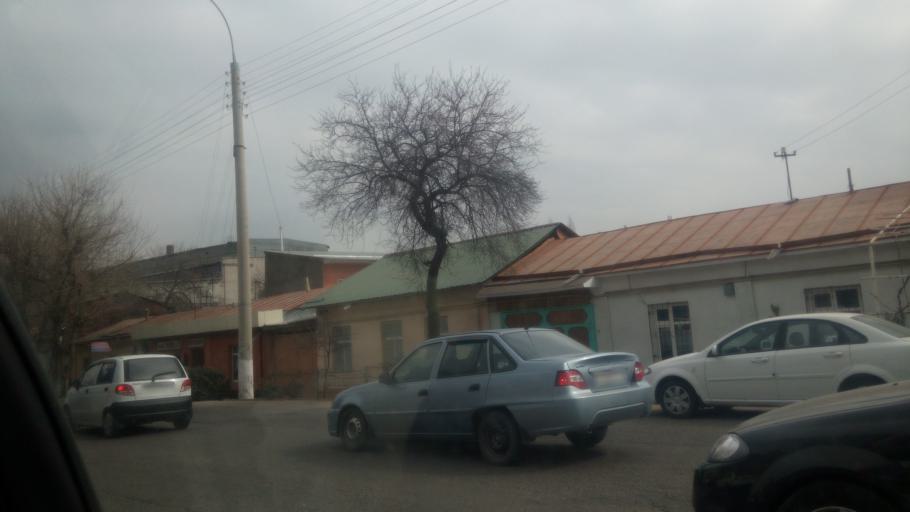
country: UZ
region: Toshkent
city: Salor
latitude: 41.3338
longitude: 69.3042
